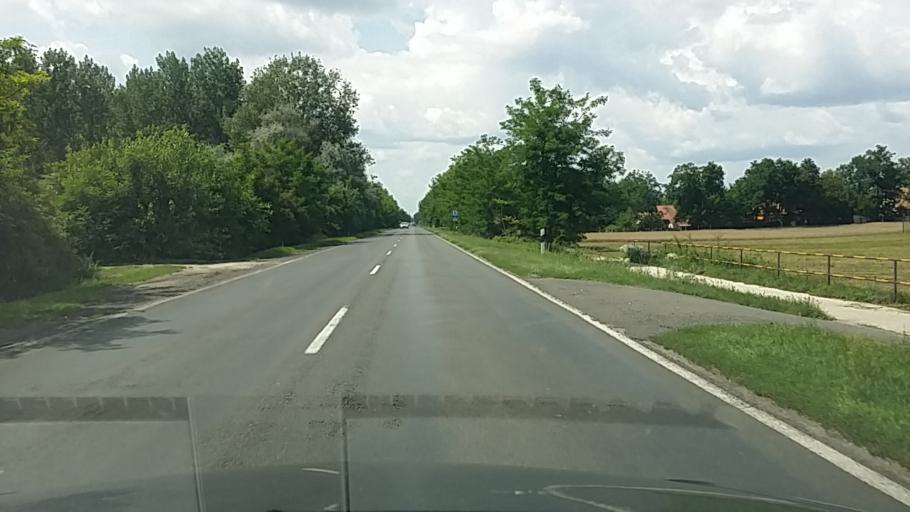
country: HU
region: Bacs-Kiskun
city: Lajosmizse
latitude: 47.0032
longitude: 19.5916
